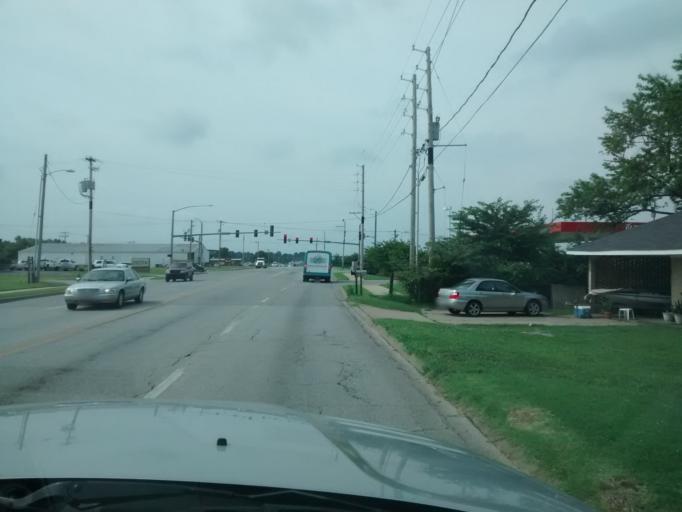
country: US
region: Arkansas
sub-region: Washington County
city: Springdale
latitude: 36.1894
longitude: -94.1163
